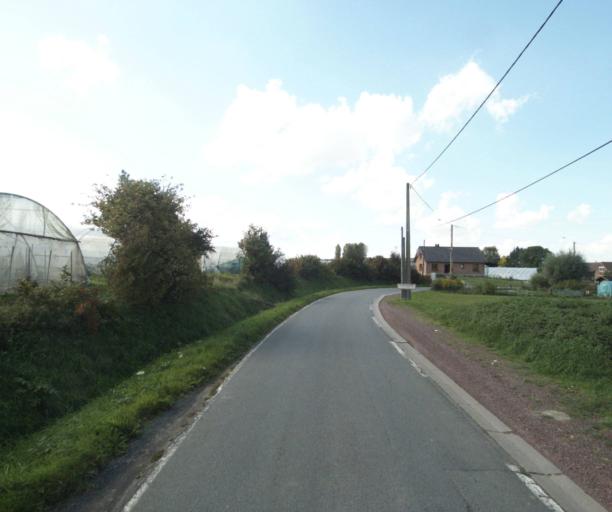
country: FR
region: Nord-Pas-de-Calais
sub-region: Departement du Nord
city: Illies
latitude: 50.5594
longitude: 2.8212
